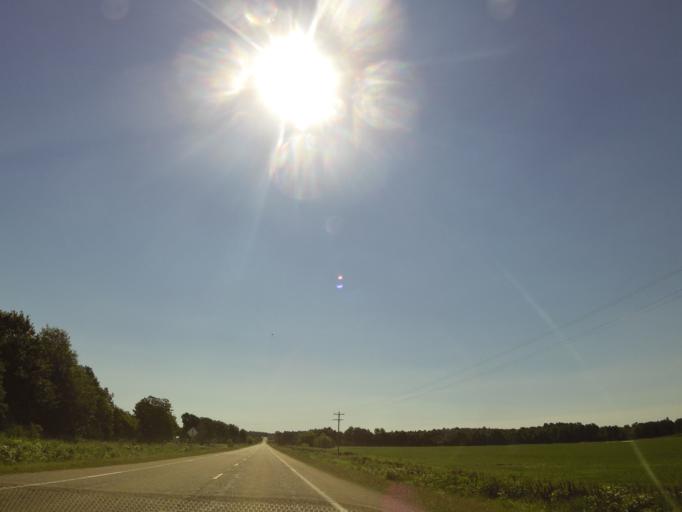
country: US
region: Arkansas
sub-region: Clay County
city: Piggott
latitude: 36.4337
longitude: -90.3475
